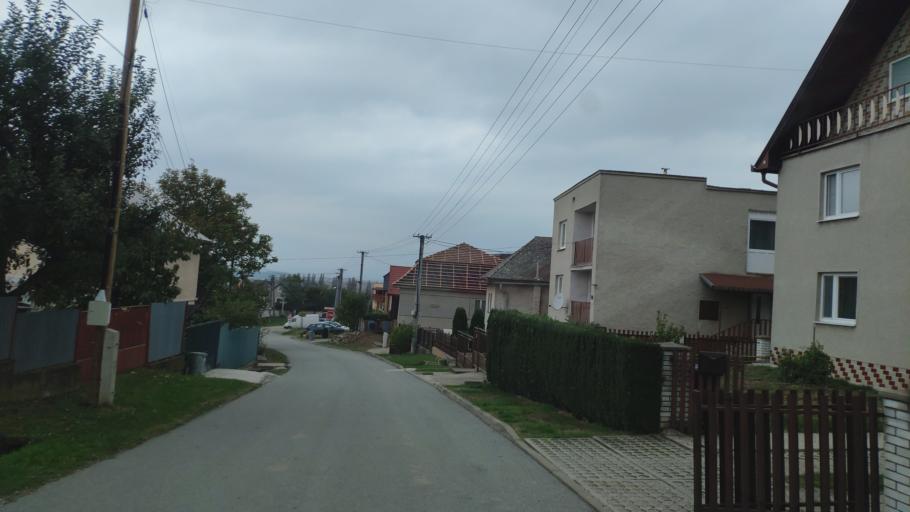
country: SK
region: Kosicky
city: Kosice
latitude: 48.6364
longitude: 21.3849
